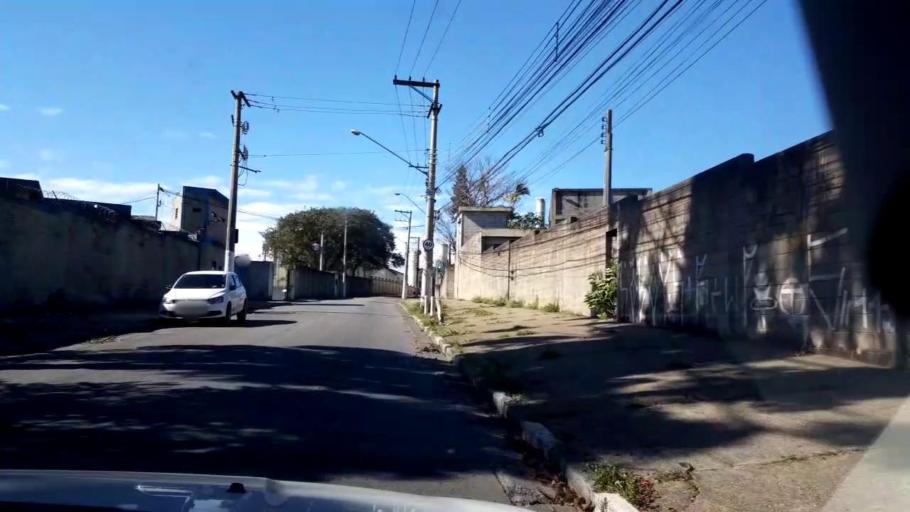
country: BR
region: Sao Paulo
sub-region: Ferraz De Vasconcelos
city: Ferraz de Vasconcelos
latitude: -23.5287
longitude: -46.3878
